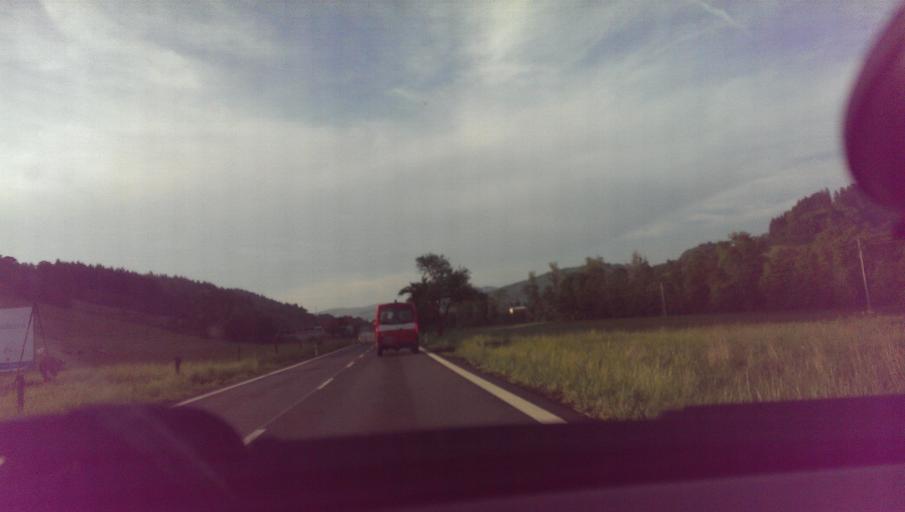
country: CZ
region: Zlin
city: Valasska Polanka
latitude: 49.2943
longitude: 18.0010
